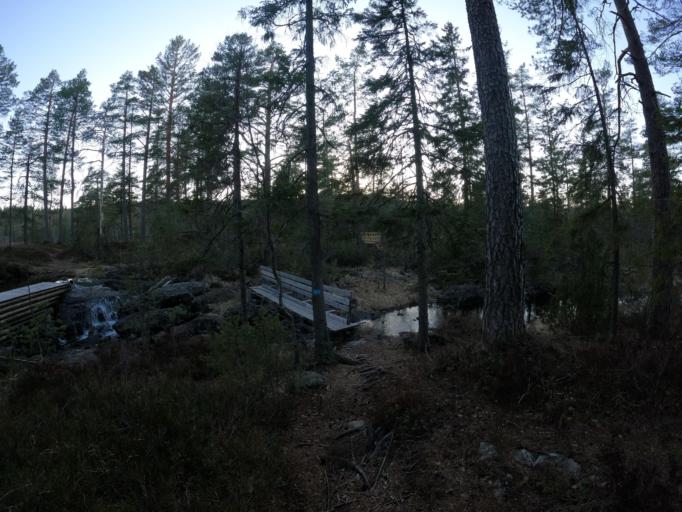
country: NO
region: Akershus
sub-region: Nittedal
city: Aneby
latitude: 60.1277
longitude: 10.9145
